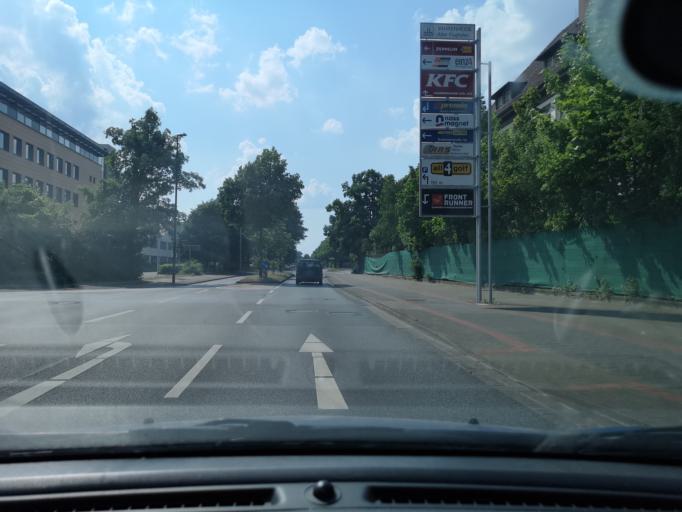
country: DE
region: Lower Saxony
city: Langenhagen
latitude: 52.4210
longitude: 9.7391
